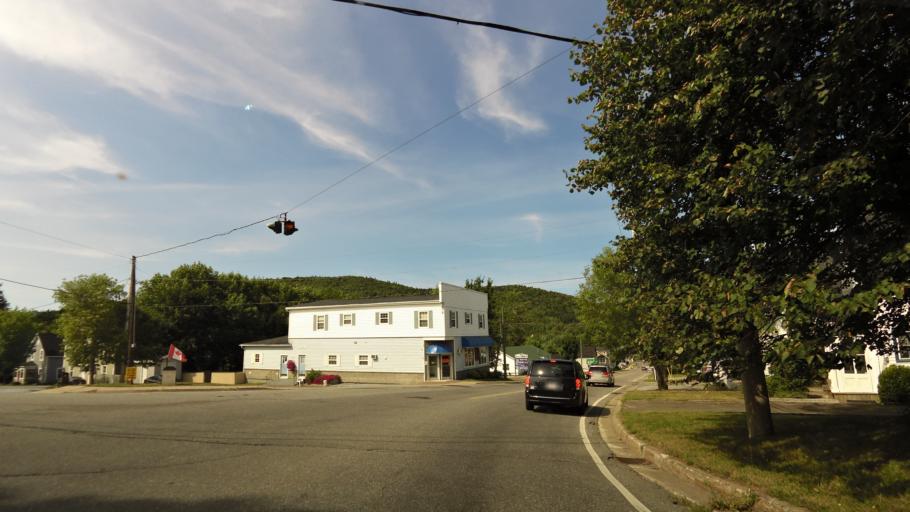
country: CA
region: New Brunswick
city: Hampton
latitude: 45.5394
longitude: -65.8358
